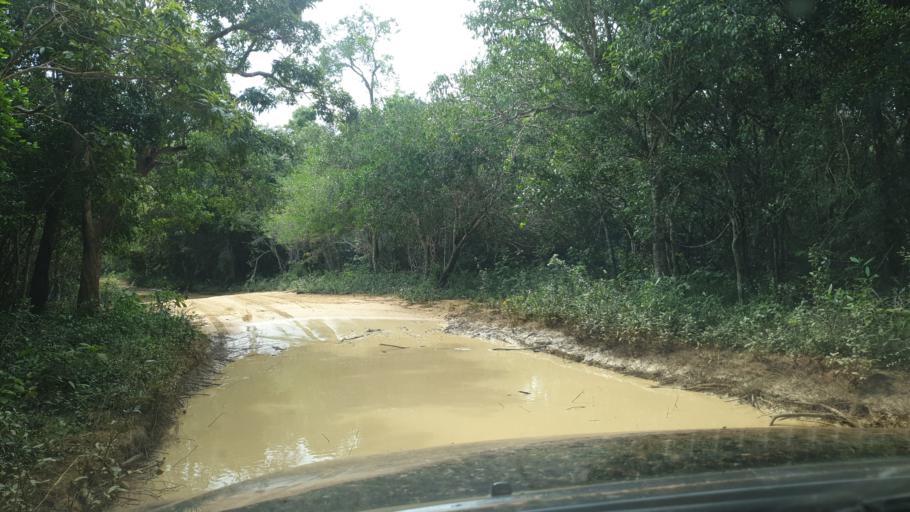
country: LK
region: North Western
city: Puttalam
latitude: 8.4184
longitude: 80.0015
